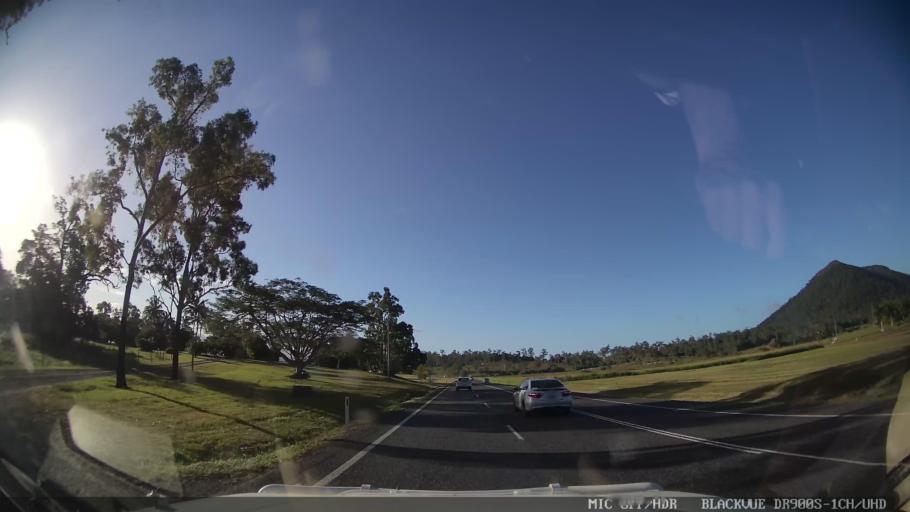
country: AU
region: Queensland
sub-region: Whitsunday
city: Proserpine
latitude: -20.3620
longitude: 148.6222
